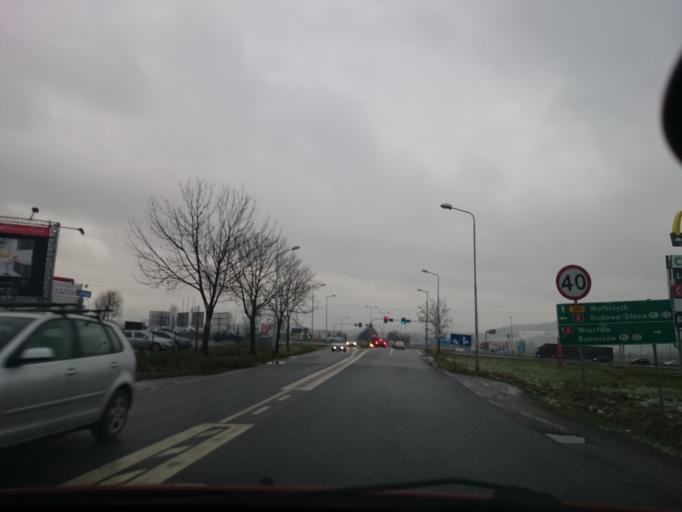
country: PL
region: Lower Silesian Voivodeship
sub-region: Powiat klodzki
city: Klodzko
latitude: 50.4522
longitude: 16.6365
